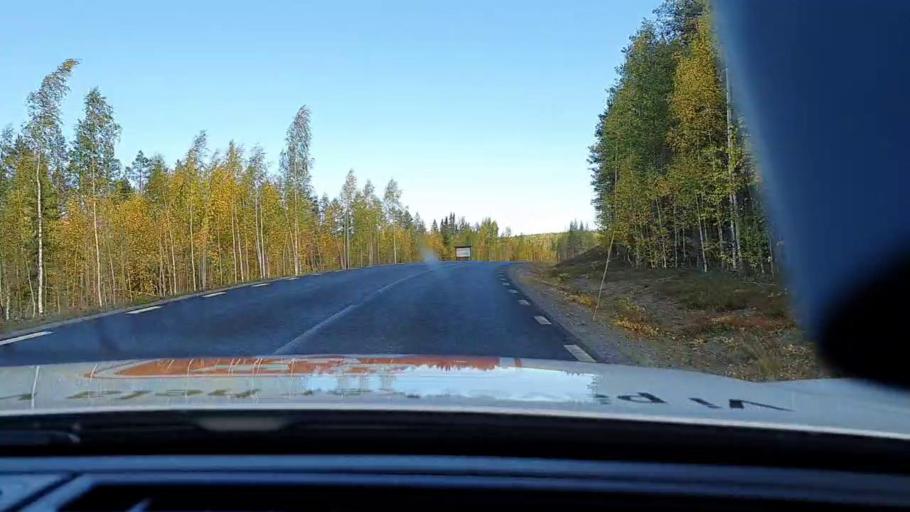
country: SE
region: Vaesterbotten
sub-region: Skelleftea Kommun
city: Langsele
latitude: 64.9498
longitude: 20.0234
